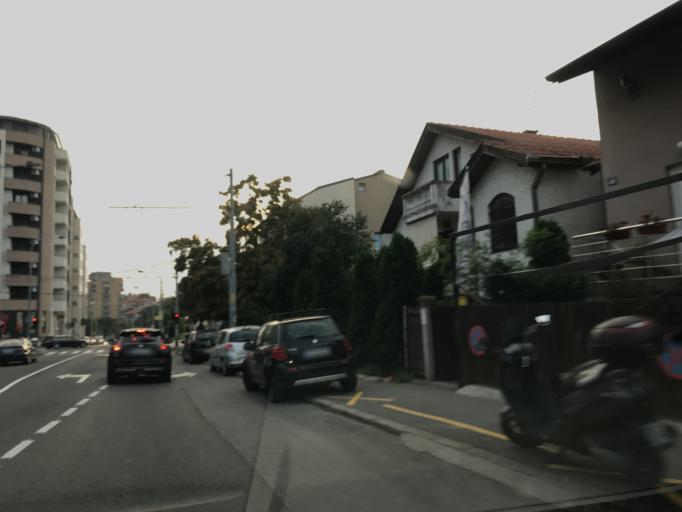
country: RS
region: Central Serbia
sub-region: Belgrade
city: Palilula
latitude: 44.7882
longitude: 20.5068
